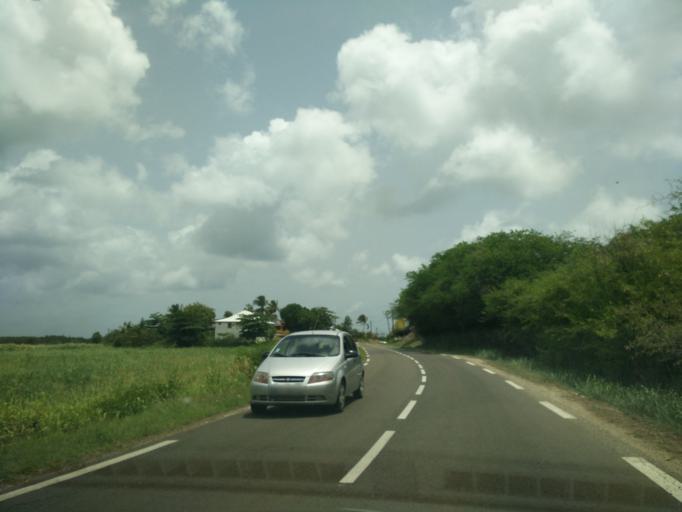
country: GP
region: Guadeloupe
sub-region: Guadeloupe
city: Port-Louis
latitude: 16.4396
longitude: -61.5129
